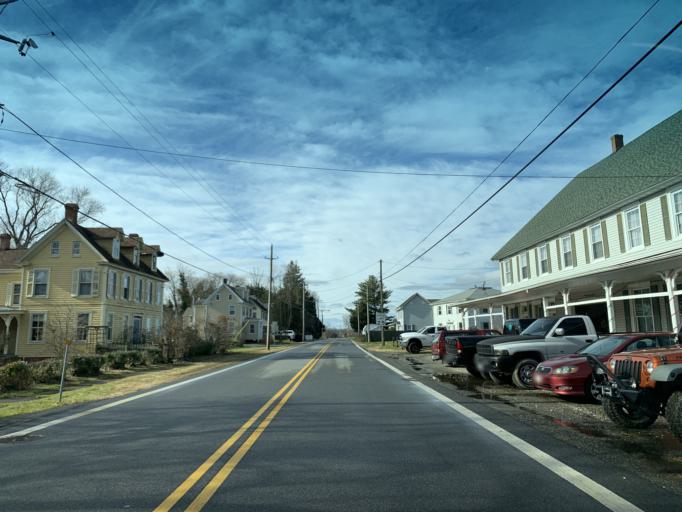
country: US
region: Maryland
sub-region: Kent County
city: Chestertown
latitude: 39.3277
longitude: -76.0456
